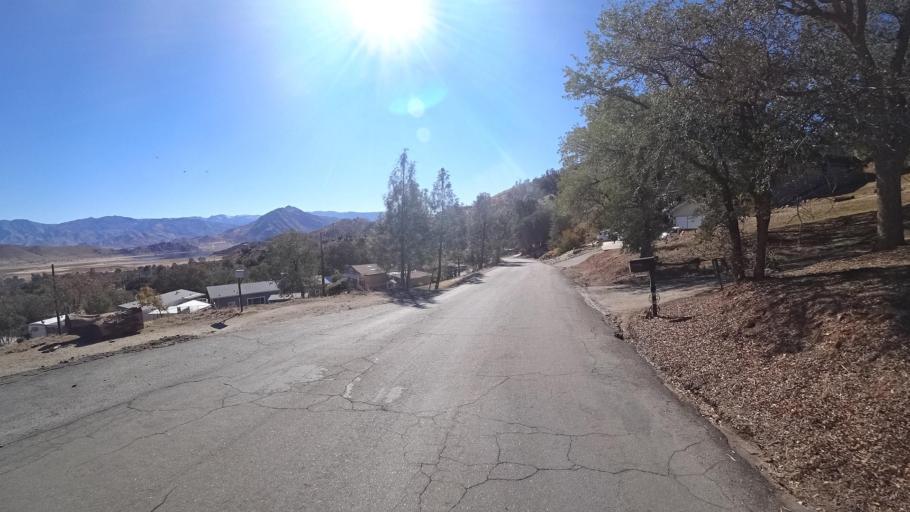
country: US
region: California
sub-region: Kern County
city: Wofford Heights
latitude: 35.7056
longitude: -118.4650
